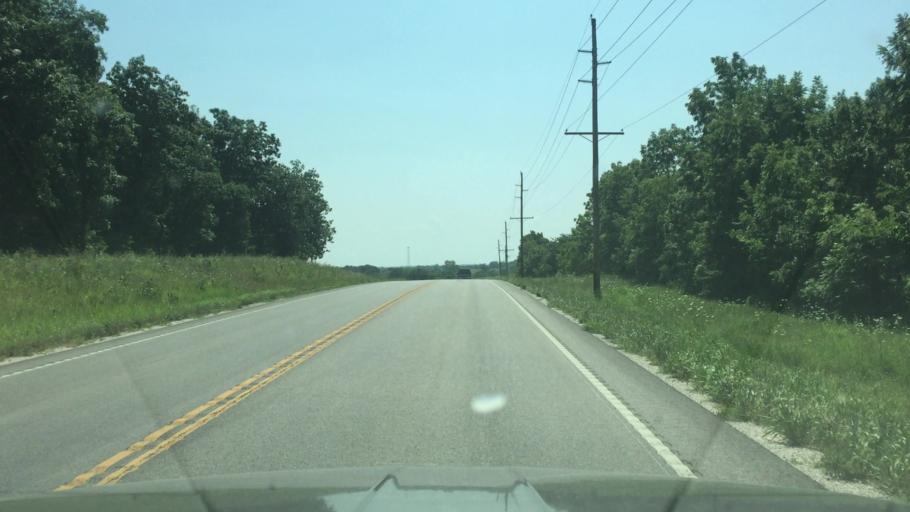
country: US
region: Missouri
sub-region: Miller County
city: Eldon
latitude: 38.3873
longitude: -92.6948
